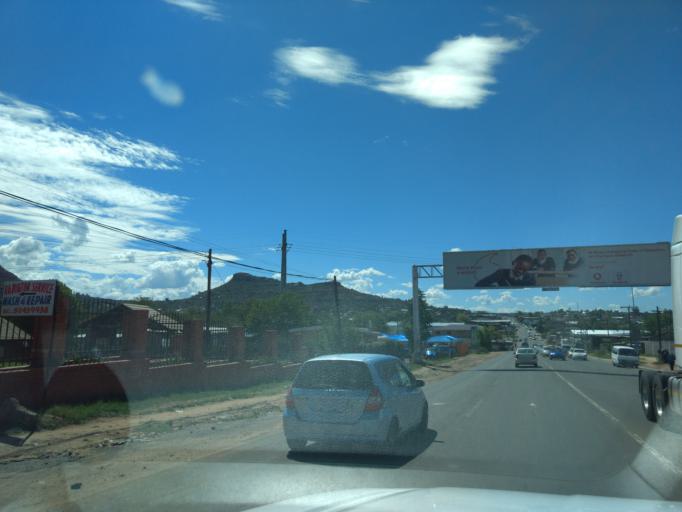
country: LS
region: Maseru
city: Maseru
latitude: -29.3463
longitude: 27.5173
